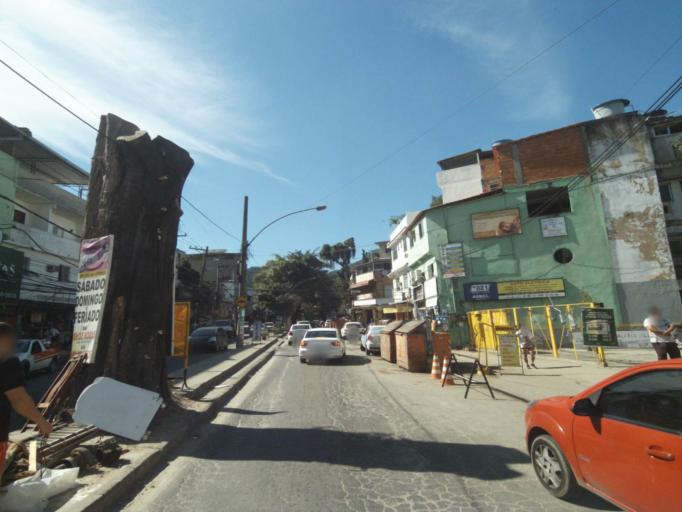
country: BR
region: Rio de Janeiro
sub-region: Rio De Janeiro
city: Rio de Janeiro
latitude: -22.9876
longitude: -43.3091
